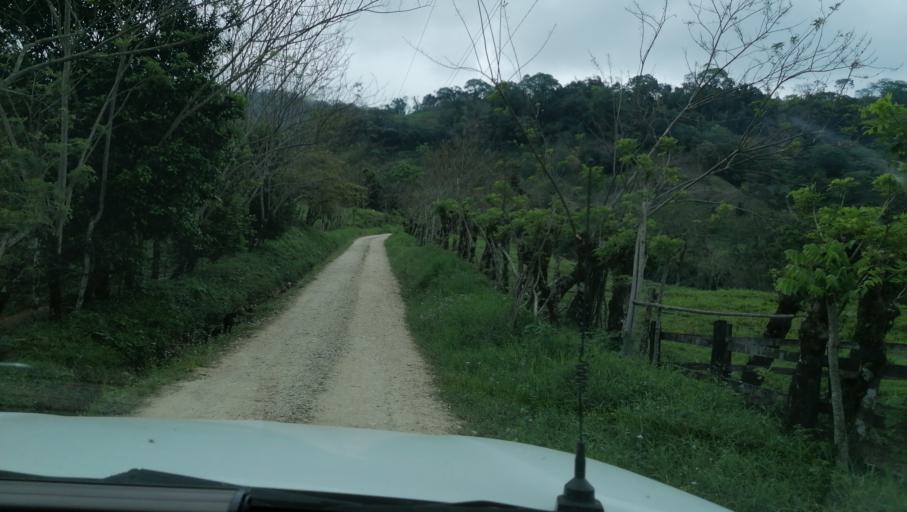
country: MX
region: Chiapas
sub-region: Ocotepec
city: San Pablo Huacano
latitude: 17.2738
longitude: -93.2403
